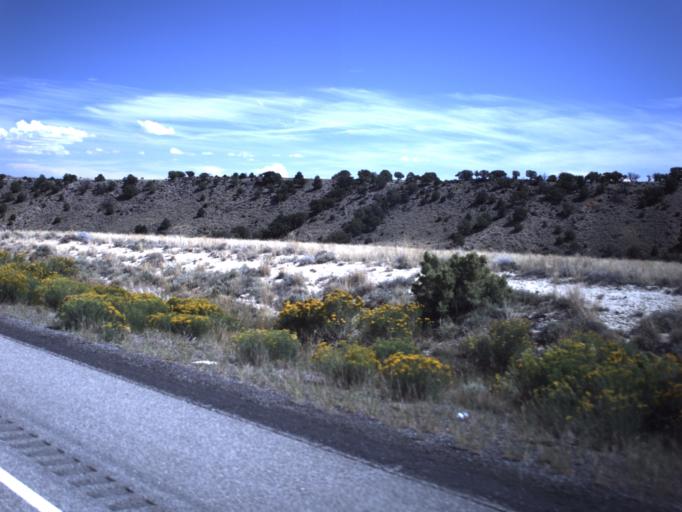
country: US
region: Utah
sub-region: Emery County
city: Ferron
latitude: 38.7802
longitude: -111.3107
